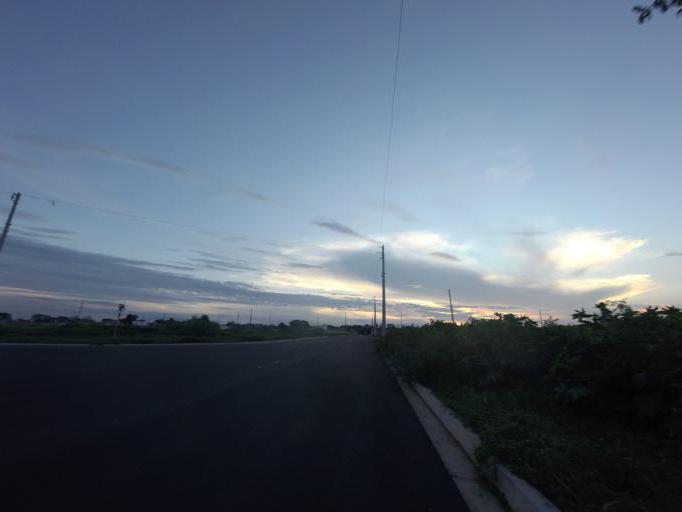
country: BR
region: Sao Paulo
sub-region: Piracicaba
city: Piracicaba
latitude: -22.7644
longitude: -47.5858
